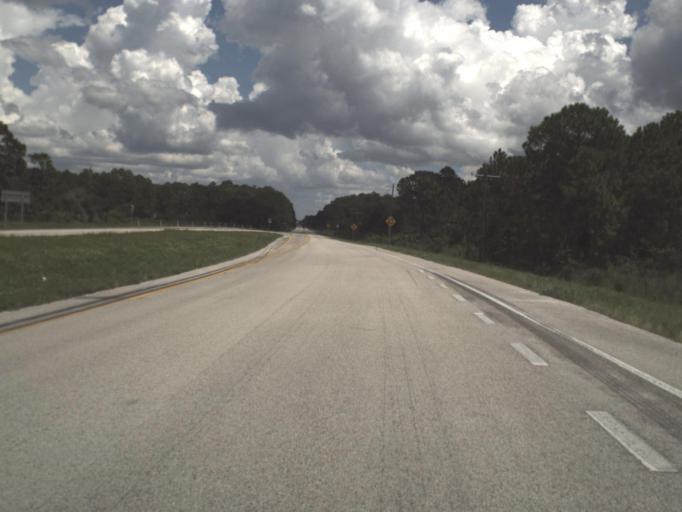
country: US
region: Florida
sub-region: Polk County
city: Babson Park
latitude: 27.8059
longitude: -81.3147
